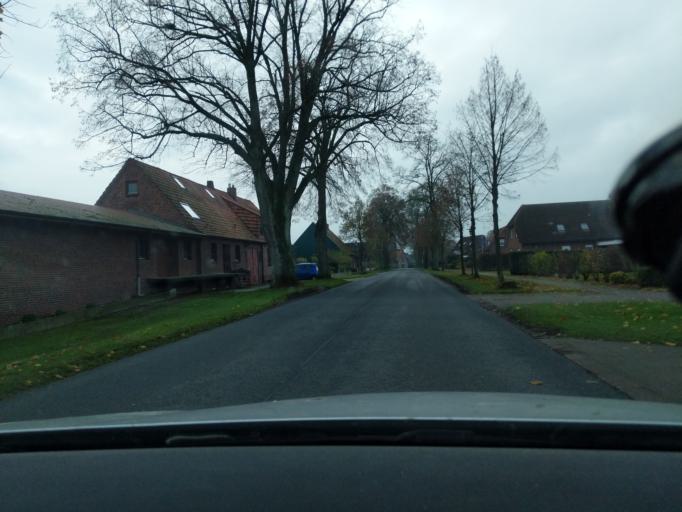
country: DE
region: Lower Saxony
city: Ahlerstedt
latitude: 53.3805
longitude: 9.4703
